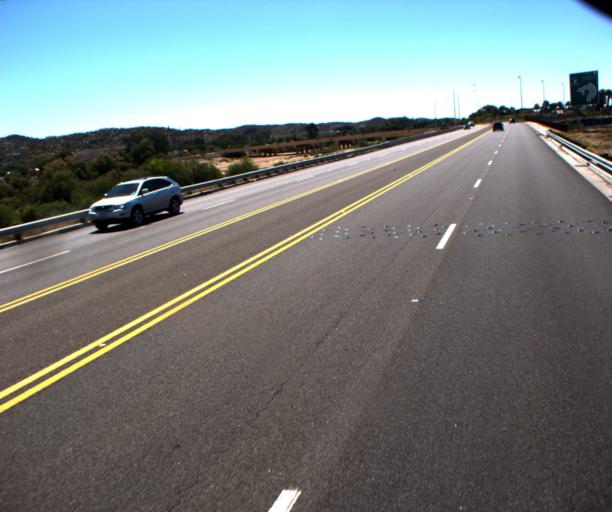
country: US
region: Arizona
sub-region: Maricopa County
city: Wickenburg
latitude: 33.9730
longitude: -112.7300
